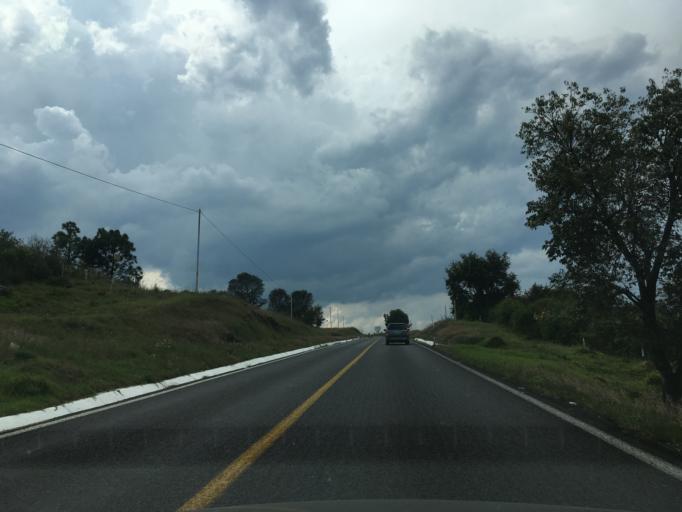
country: MX
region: Michoacan
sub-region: Patzcuaro
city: Santa Ana Chapitiro
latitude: 19.5226
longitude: -101.6588
